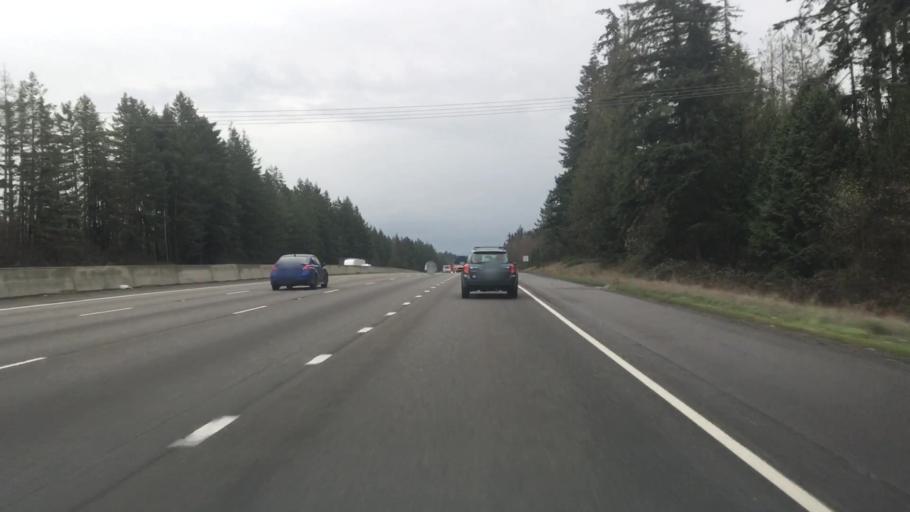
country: US
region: Washington
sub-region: Thurston County
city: Grand Mound
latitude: 46.8804
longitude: -122.9663
